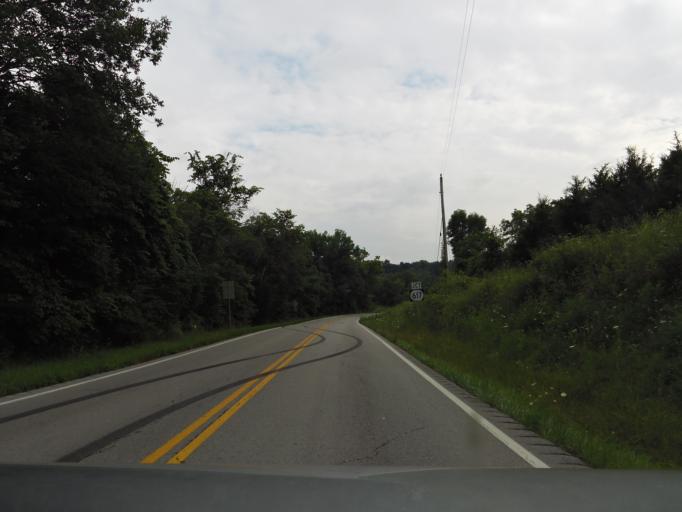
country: US
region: Kentucky
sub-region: Robertson County
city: Mount Olivet
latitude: 38.4945
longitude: -84.1091
